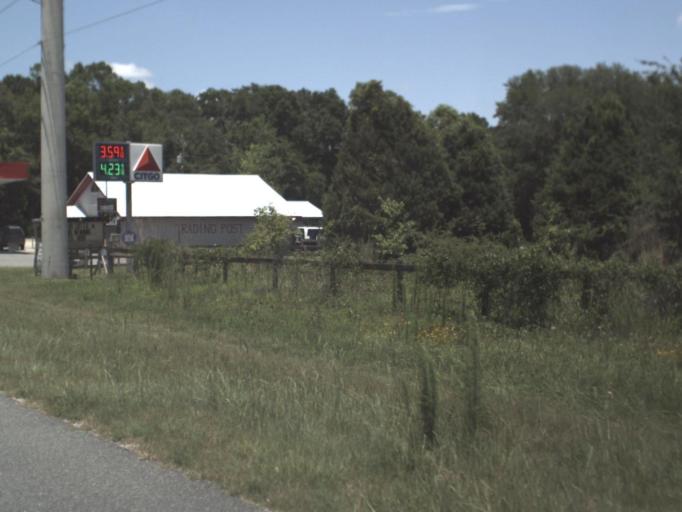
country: US
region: Florida
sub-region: Dixie County
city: Cross City
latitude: 29.6822
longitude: -82.9842
